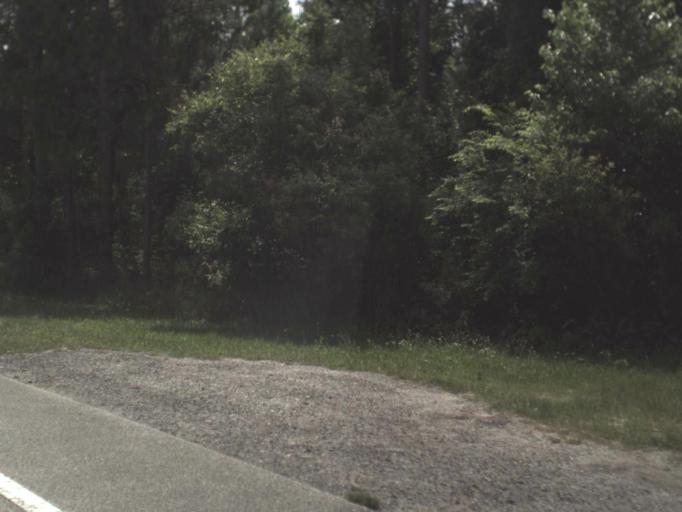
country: US
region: Florida
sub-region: Saint Johns County
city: Saint Augustine Shores
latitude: 29.7323
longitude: -81.3847
